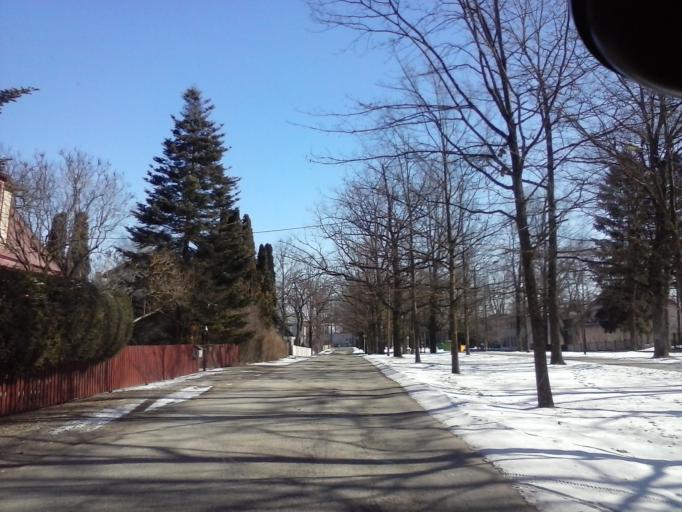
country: EE
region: Tartu
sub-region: Tartu linn
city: Tartu
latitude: 58.3647
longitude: 26.7088
